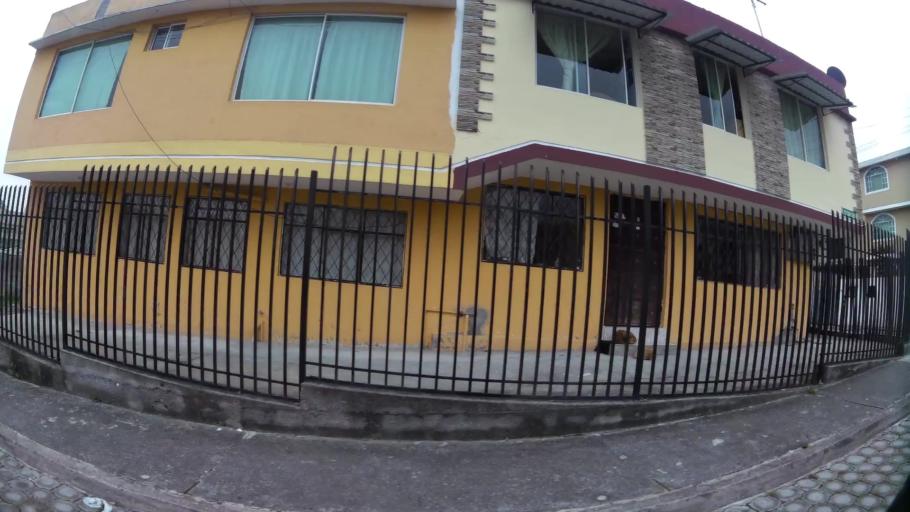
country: EC
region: Pichincha
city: Quito
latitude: -0.2651
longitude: -78.4749
